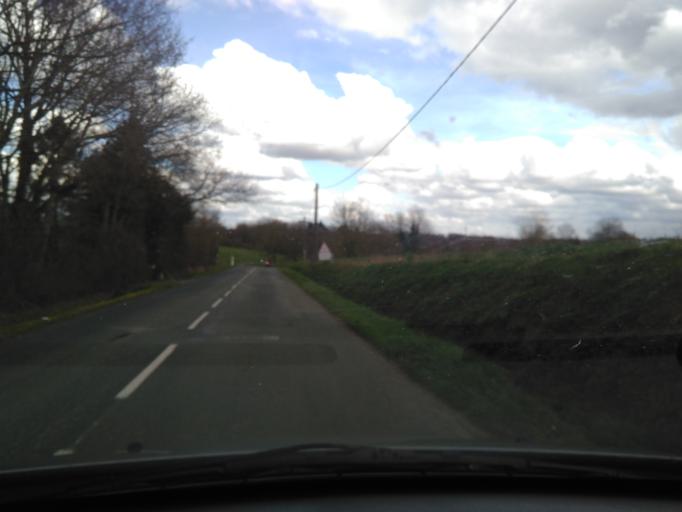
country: FR
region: Pays de la Loire
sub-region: Departement de la Vendee
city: Sainte-Cecile
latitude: 46.6882
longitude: -1.1228
